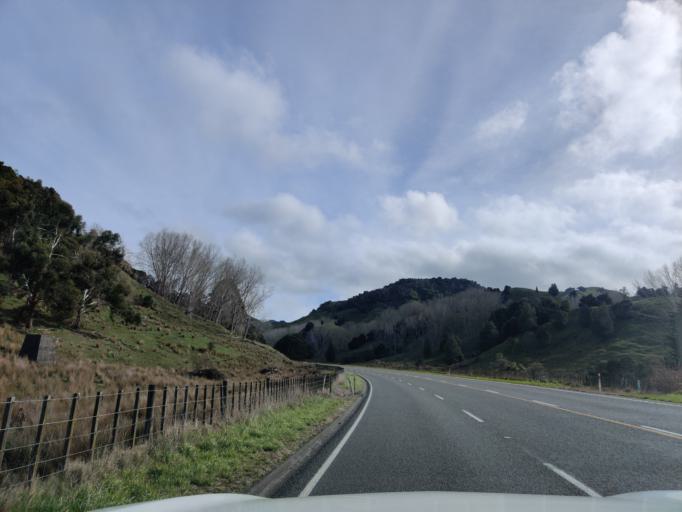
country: NZ
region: Manawatu-Wanganui
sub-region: Ruapehu District
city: Waiouru
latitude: -39.8005
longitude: 175.7979
